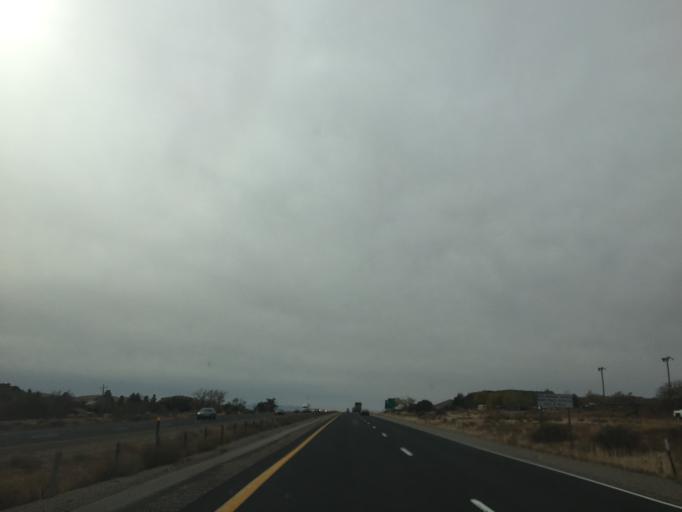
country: US
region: Utah
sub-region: Washington County
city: Toquerville
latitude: 37.2488
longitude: -113.3461
